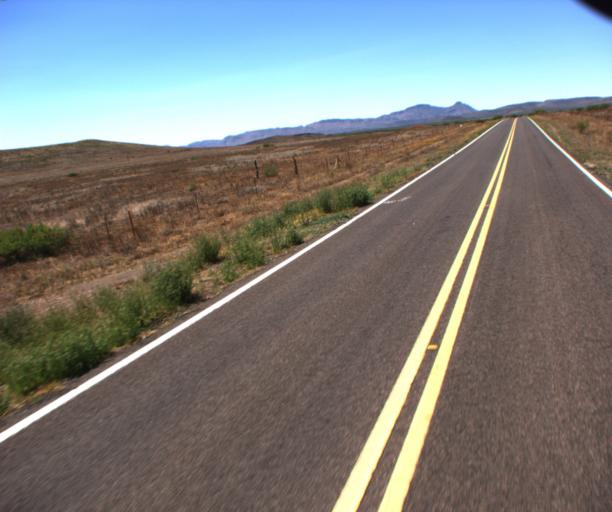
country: US
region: Arizona
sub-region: Cochise County
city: Douglas
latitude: 31.5494
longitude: -109.2759
